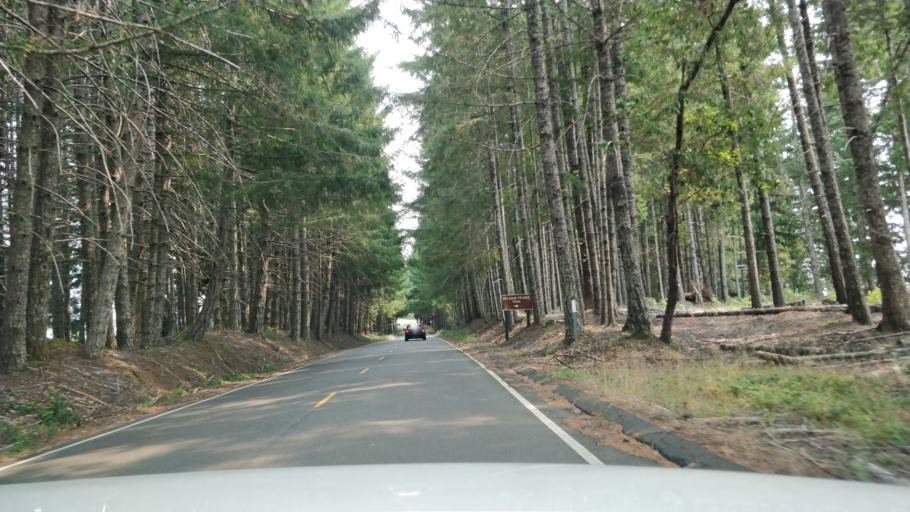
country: US
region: California
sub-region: Humboldt County
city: Westhaven-Moonstone
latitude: 41.2064
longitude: -123.9516
